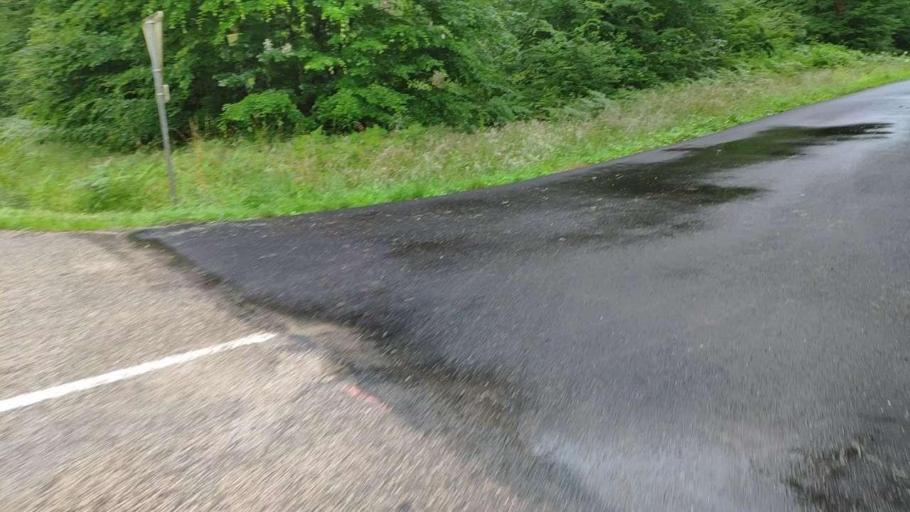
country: FR
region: Franche-Comte
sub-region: Departement du Jura
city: Chaussin
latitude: 46.8894
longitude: 5.4283
